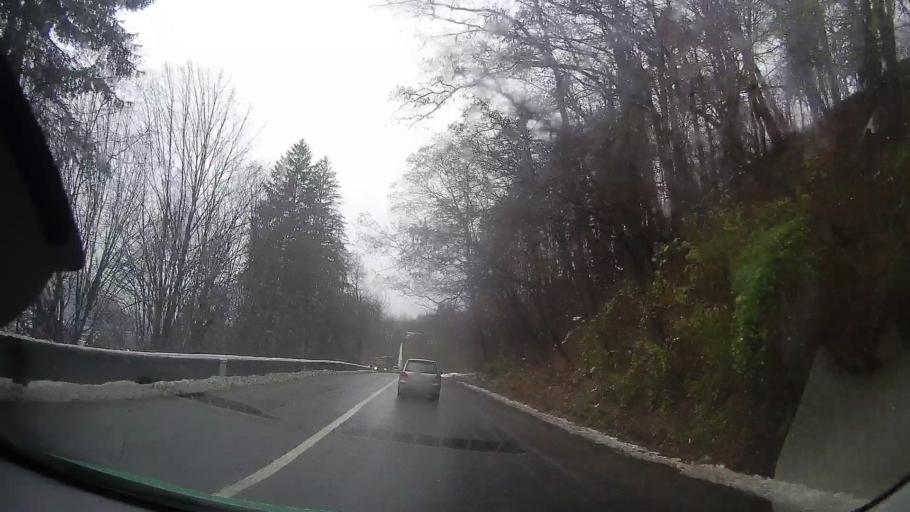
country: RO
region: Neamt
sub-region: Comuna Bicaz
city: Dodeni
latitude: 46.9002
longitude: 26.1187
